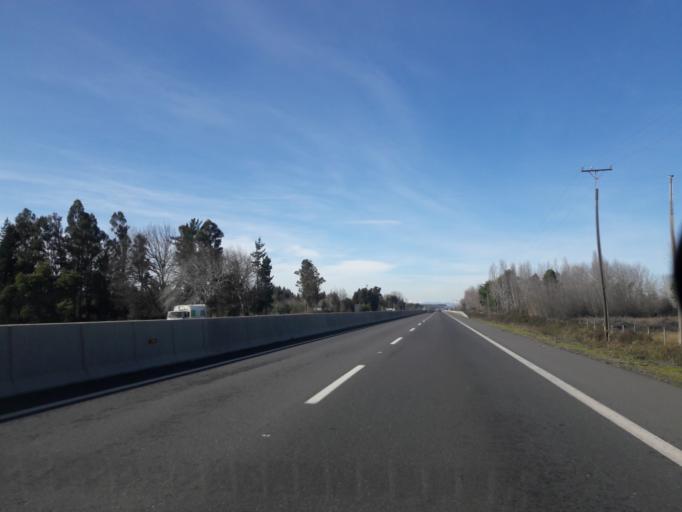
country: CL
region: Biobio
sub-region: Provincia de Biobio
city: Cabrero
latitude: -37.0251
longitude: -72.4562
